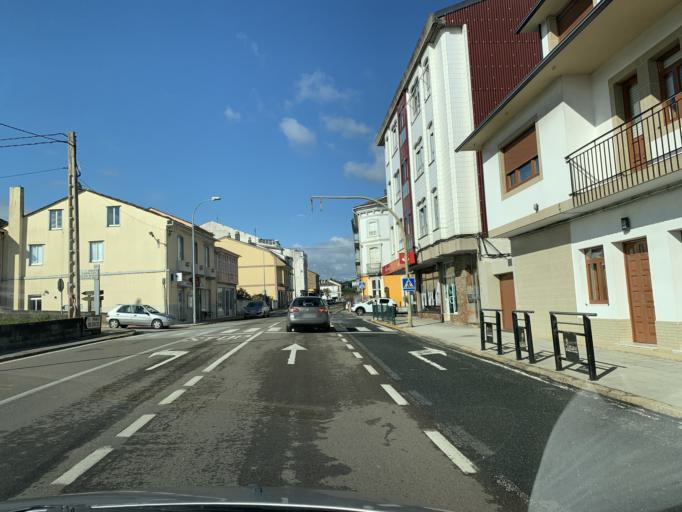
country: ES
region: Galicia
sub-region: Provincia de Lugo
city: Barreiros
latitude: 43.5417
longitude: -7.2312
